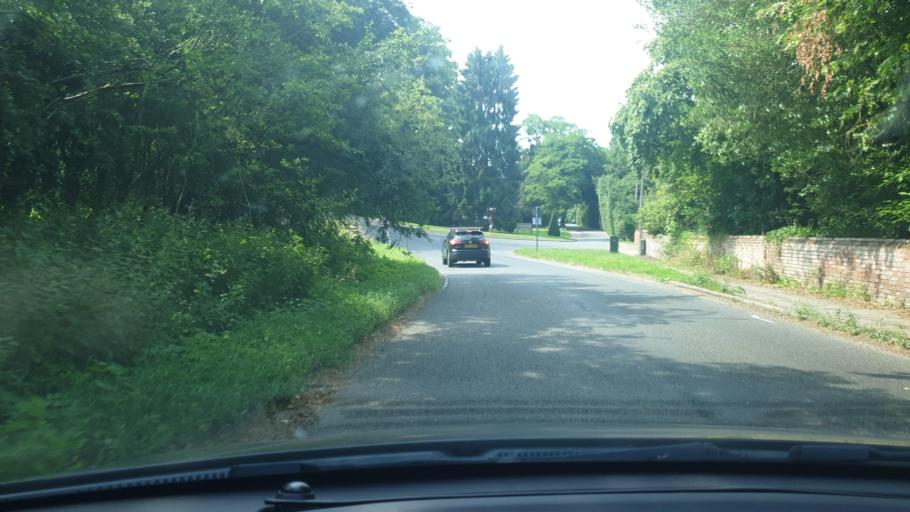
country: GB
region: England
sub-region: Suffolk
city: East Bergholt
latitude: 51.9597
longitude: 0.9748
